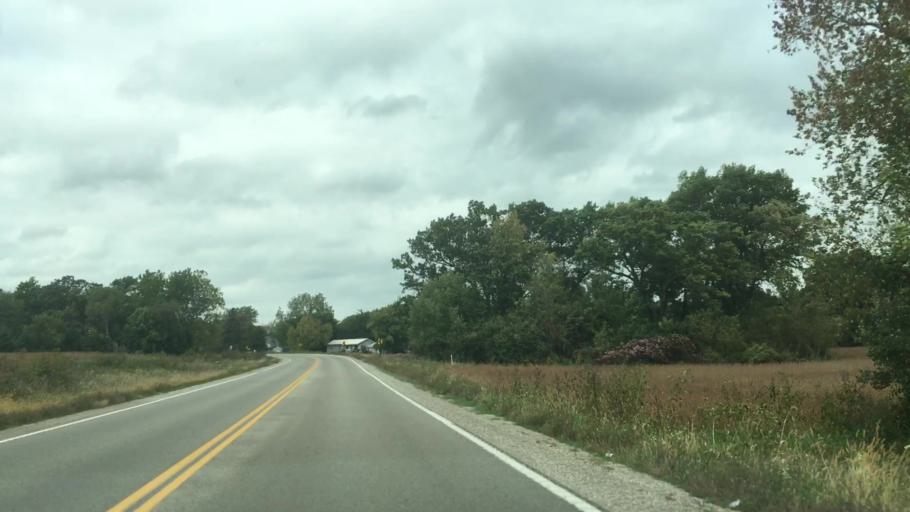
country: US
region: Minnesota
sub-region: Fillmore County
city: Preston
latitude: 43.7370
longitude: -92.1264
